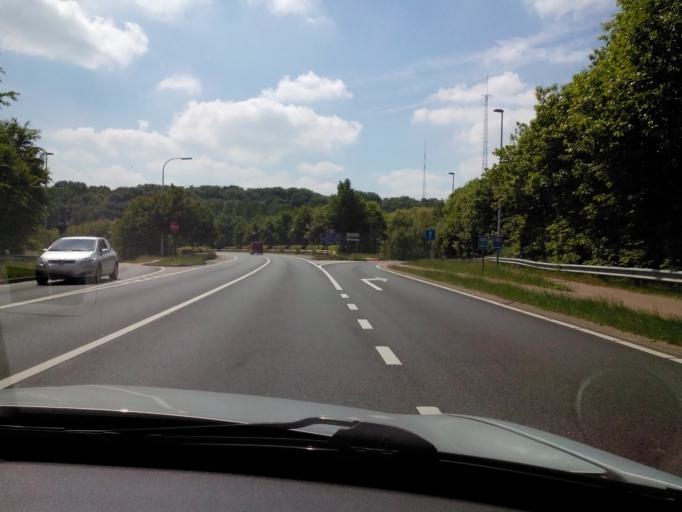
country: BE
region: Flanders
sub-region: Provincie Vlaams-Brabant
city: Aarschot
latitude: 50.9846
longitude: 4.8414
